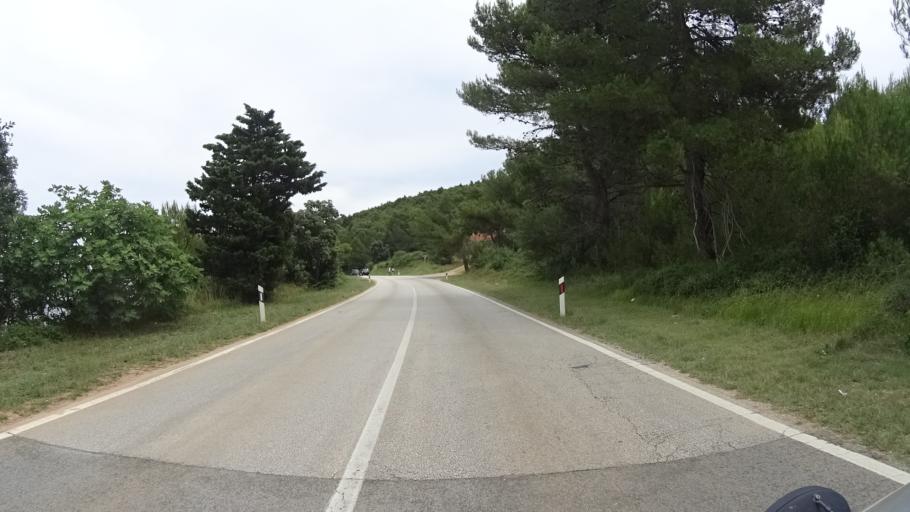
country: HR
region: Istarska
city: Medulin
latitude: 44.8148
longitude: 13.9014
